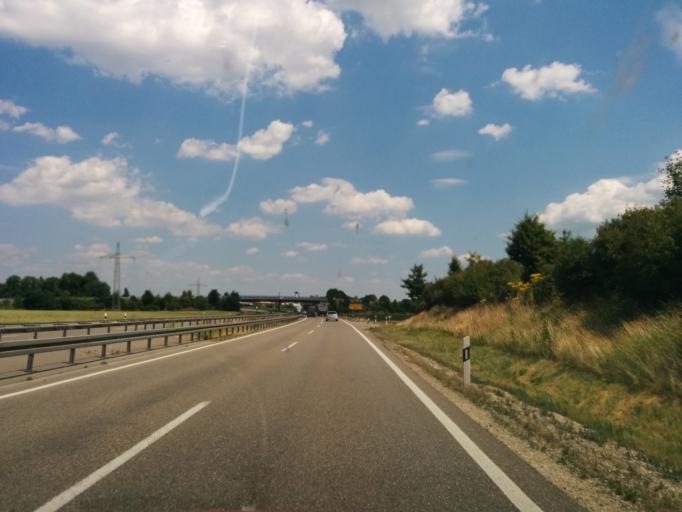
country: DE
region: Bavaria
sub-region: Swabia
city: Meitingen
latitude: 48.5370
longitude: 10.8370
